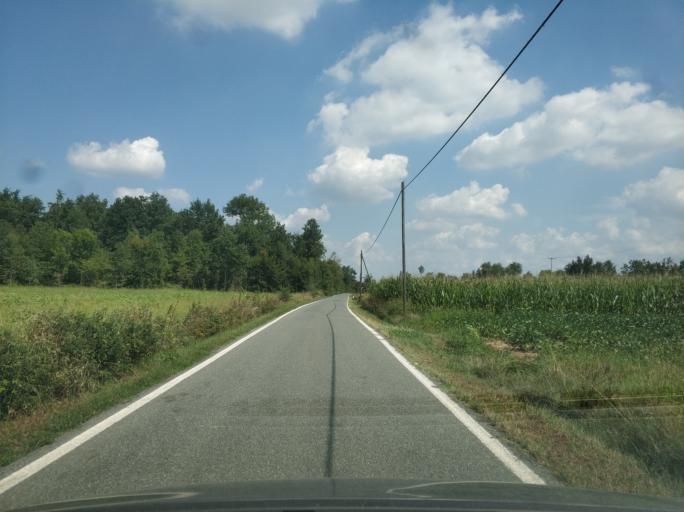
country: IT
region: Piedmont
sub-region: Provincia di Torino
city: Rivarossa
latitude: 45.2468
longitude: 7.6890
